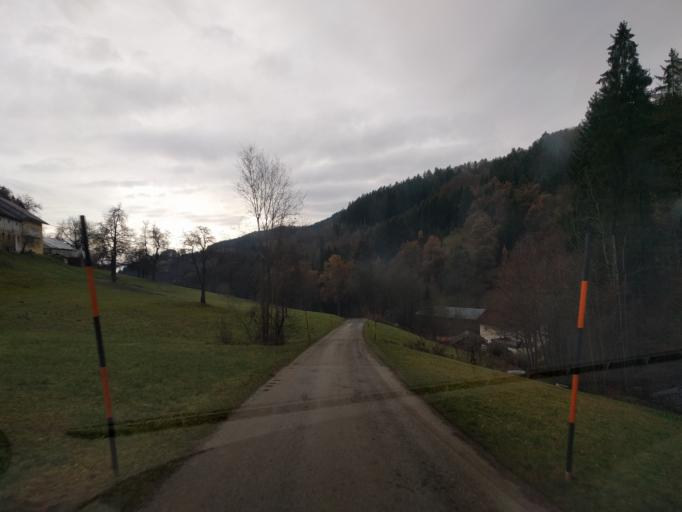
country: AT
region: Upper Austria
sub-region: Politischer Bezirk Urfahr-Umgebung
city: Hellmonsodt
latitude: 48.4199
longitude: 14.2977
